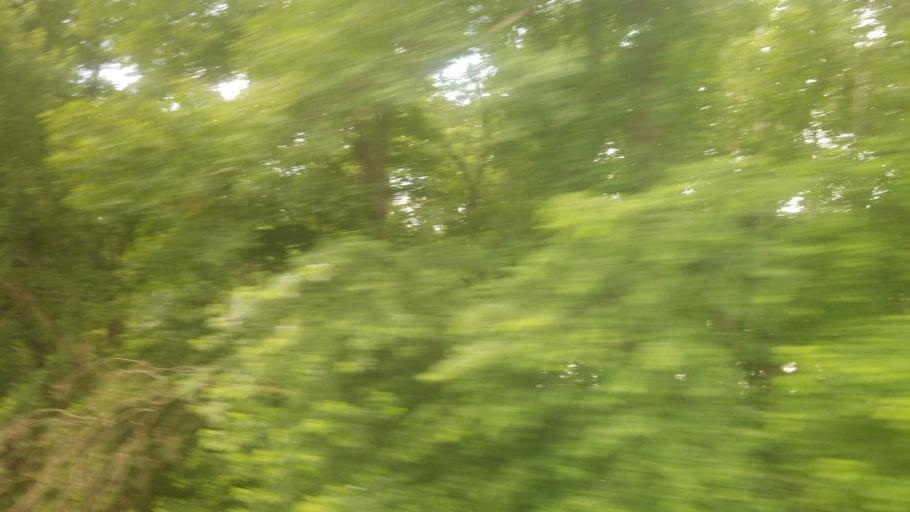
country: US
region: Maryland
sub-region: Frederick County
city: Brunswick
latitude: 39.3052
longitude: -77.5981
